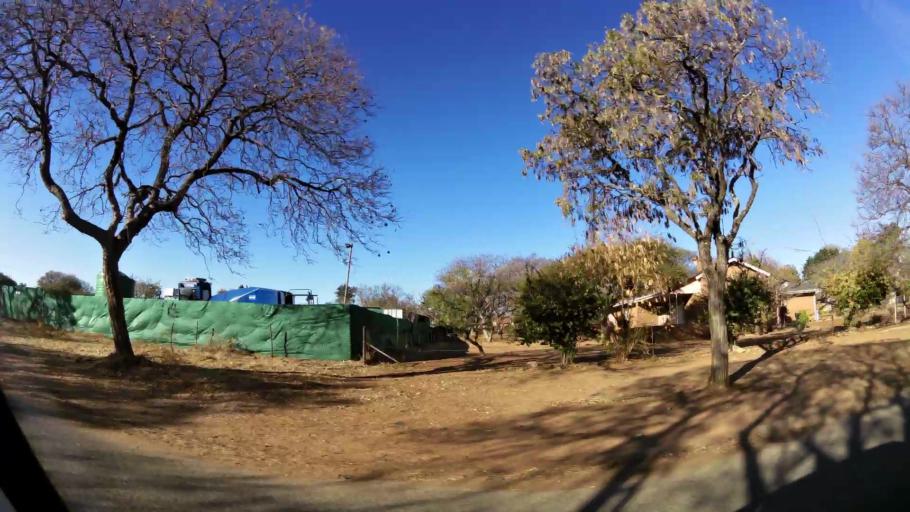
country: ZA
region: Limpopo
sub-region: Capricorn District Municipality
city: Polokwane
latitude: -23.8977
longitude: 29.4607
